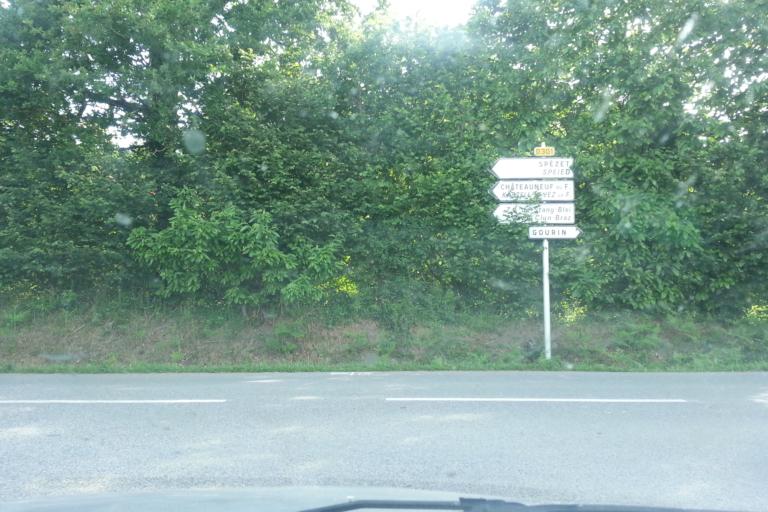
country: FR
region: Brittany
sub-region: Departement du Morbihan
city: Gourin
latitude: 48.1453
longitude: -3.6183
